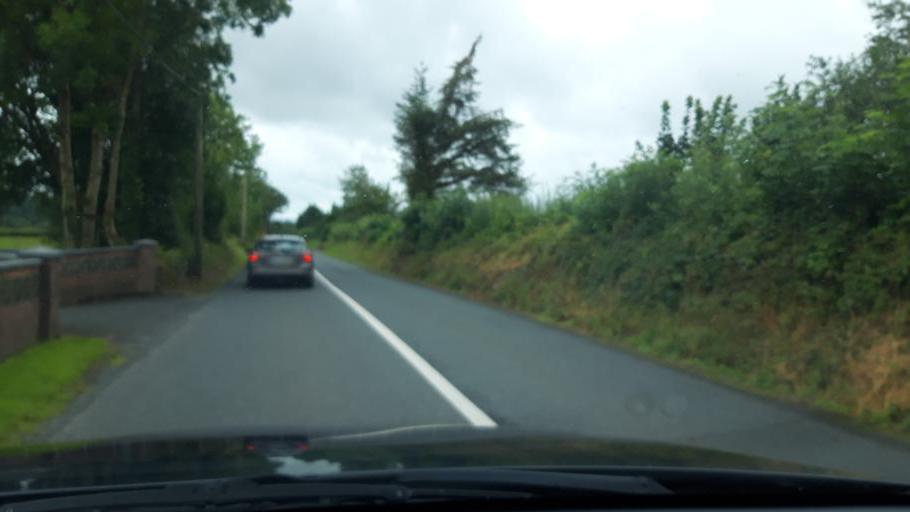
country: IE
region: Munster
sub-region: County Cork
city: Youghal
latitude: 52.1588
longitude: -7.8428
